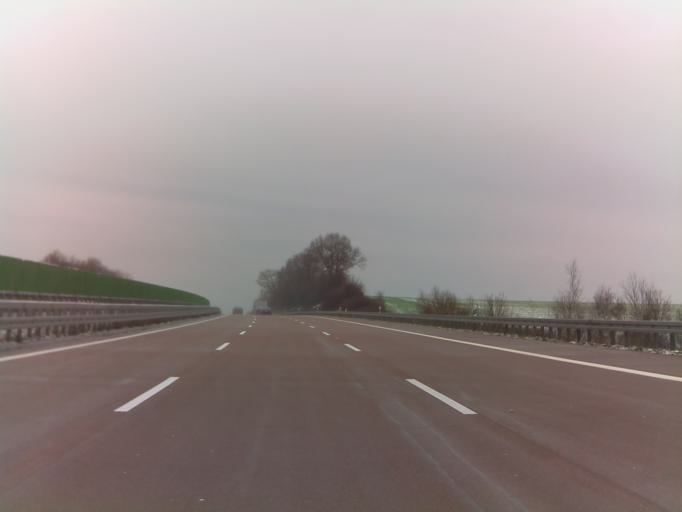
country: DE
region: Saxony-Anhalt
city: Osterfeld
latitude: 51.0687
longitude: 11.9544
